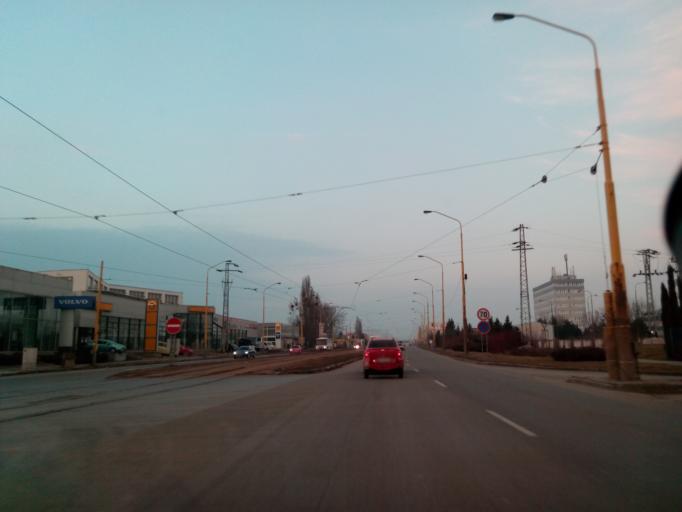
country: SK
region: Kosicky
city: Kosice
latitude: 48.6796
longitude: 21.2687
